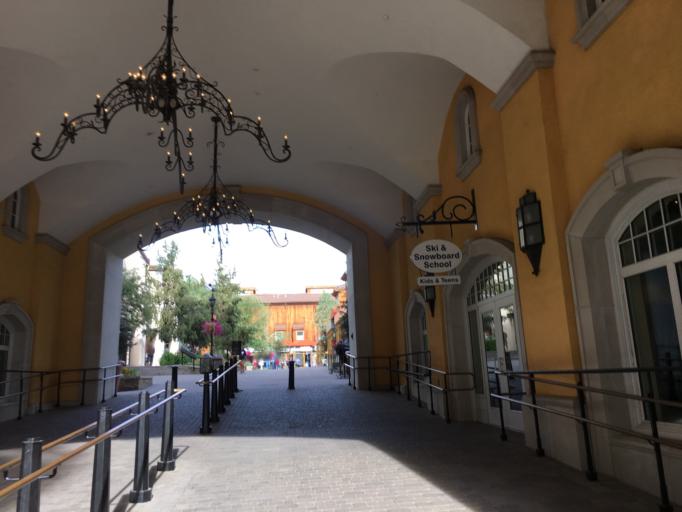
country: US
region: Colorado
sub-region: Eagle County
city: Vail
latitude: 39.6433
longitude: -106.3884
